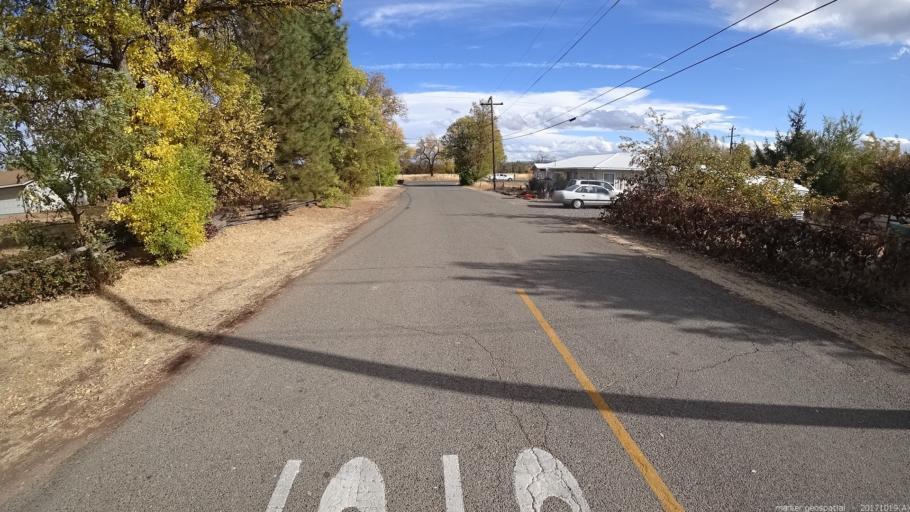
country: US
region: California
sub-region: Shasta County
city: Burney
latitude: 41.0109
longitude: -121.4360
